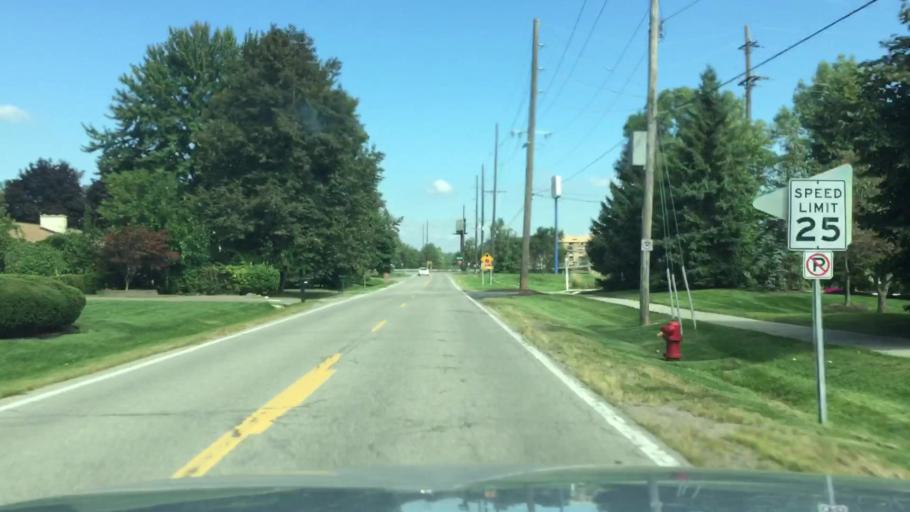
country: US
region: Michigan
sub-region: Wayne County
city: Belleville
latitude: 42.2170
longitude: -83.4942
